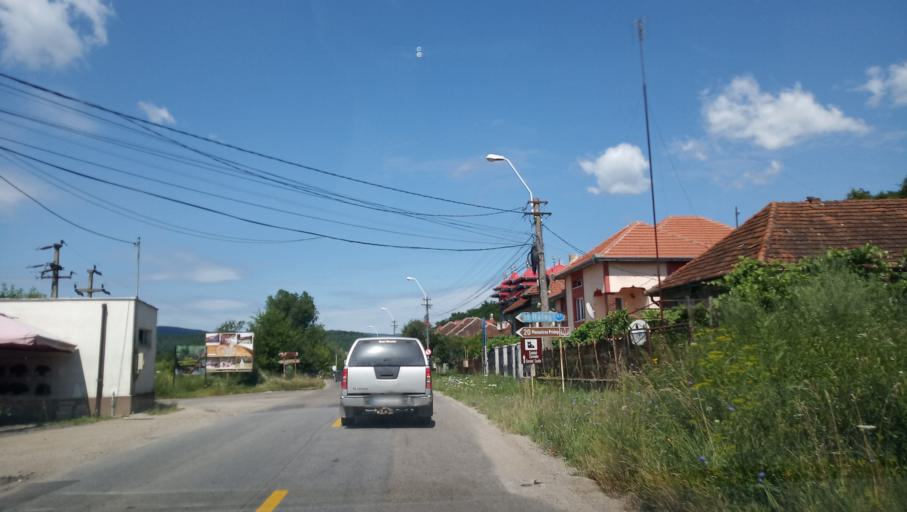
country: RO
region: Hunedoara
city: Hunedoara
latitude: 45.7360
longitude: 22.9103
